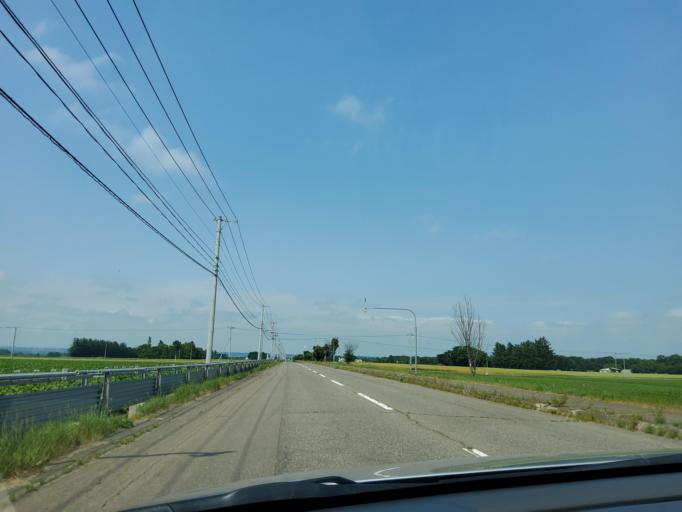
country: JP
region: Hokkaido
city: Obihiro
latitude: 42.8800
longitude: 143.0313
